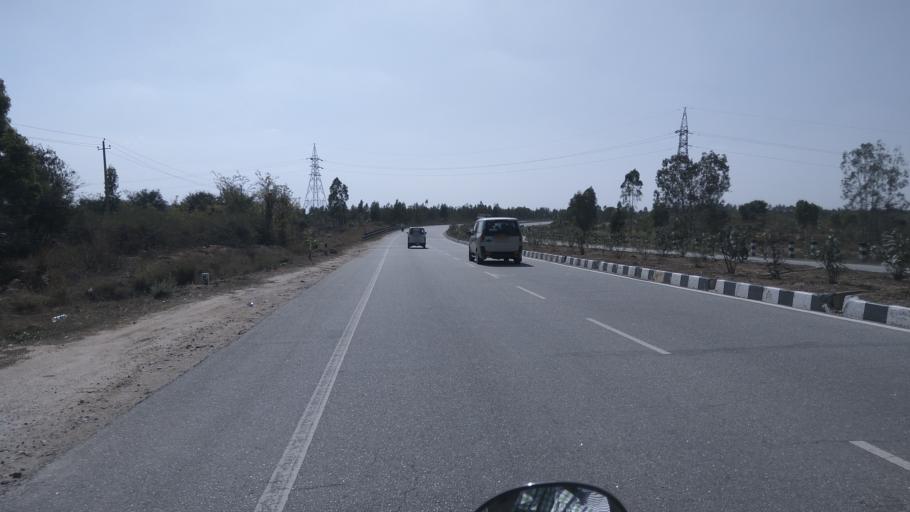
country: IN
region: Karnataka
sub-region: Kolar
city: Mulbagal
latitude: 13.1523
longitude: 78.3166
